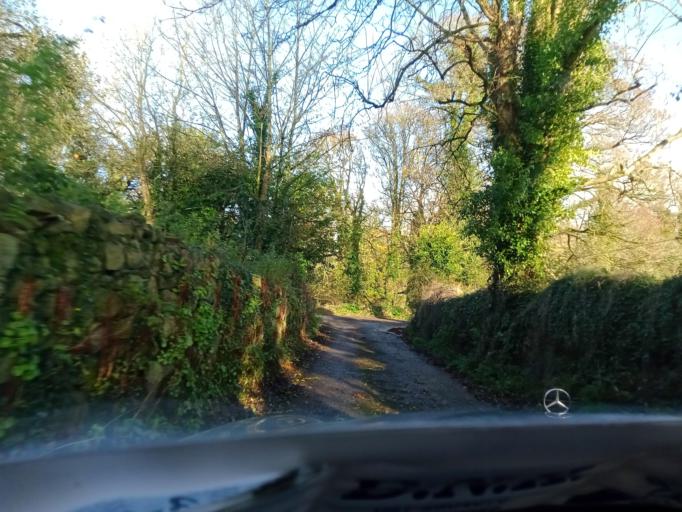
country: IE
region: Leinster
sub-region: Kilkenny
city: Mooncoin
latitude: 52.2759
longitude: -7.2397
